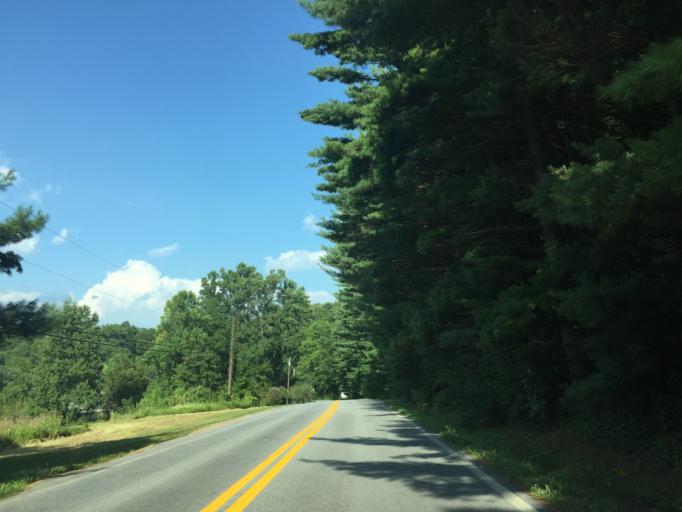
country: US
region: Maryland
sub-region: Carroll County
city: Manchester
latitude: 39.6422
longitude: -76.9147
